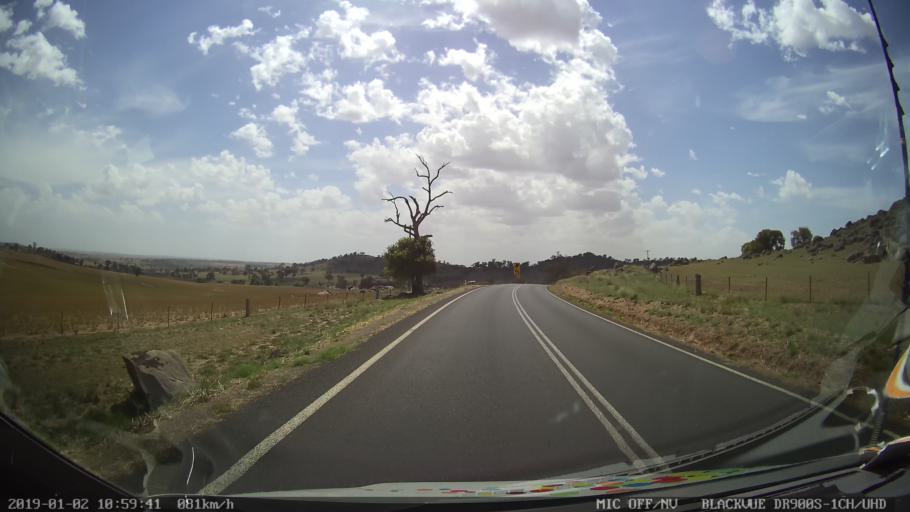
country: AU
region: New South Wales
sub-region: Cootamundra
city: Cootamundra
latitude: -34.6133
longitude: 148.3089
